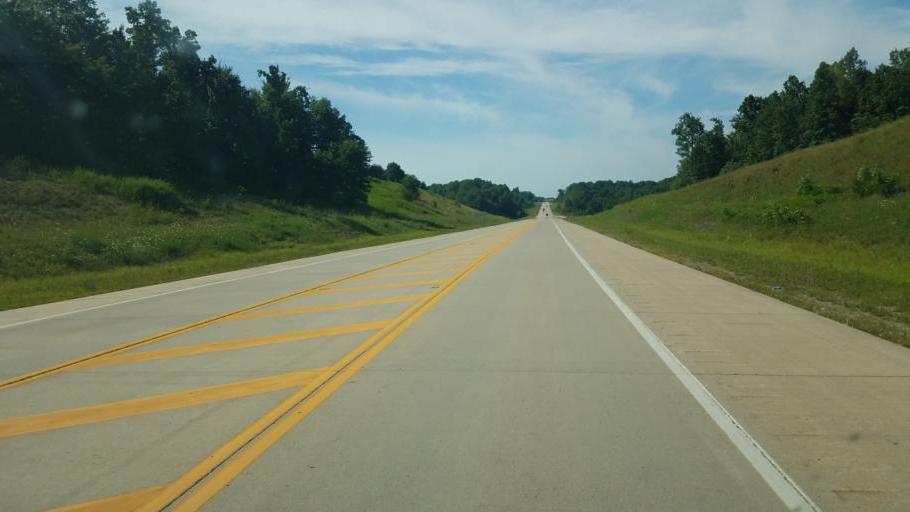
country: US
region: Ohio
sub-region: Athens County
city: Athens
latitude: 39.2394
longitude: -82.0750
